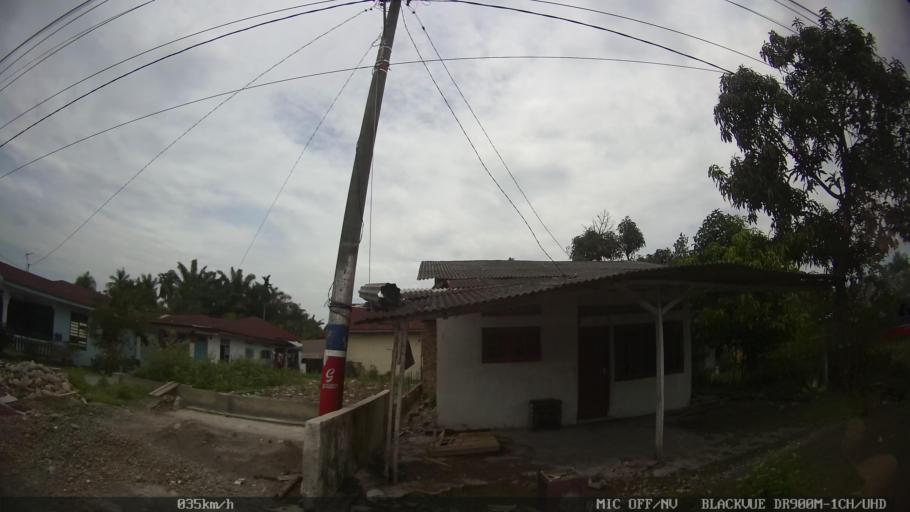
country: ID
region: North Sumatra
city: Binjai
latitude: 3.6378
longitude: 98.5527
